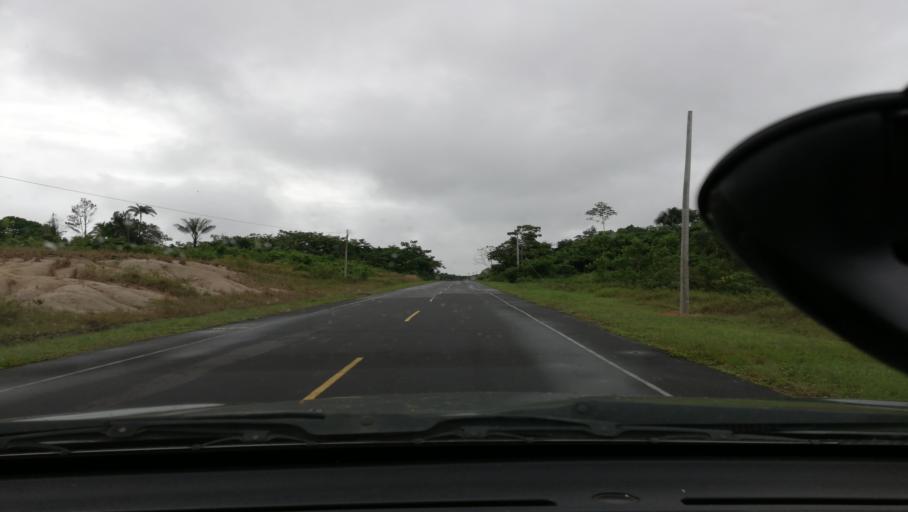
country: PE
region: Loreto
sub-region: Provincia de Loreto
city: Nauta
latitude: -4.3357
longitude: -73.5357
